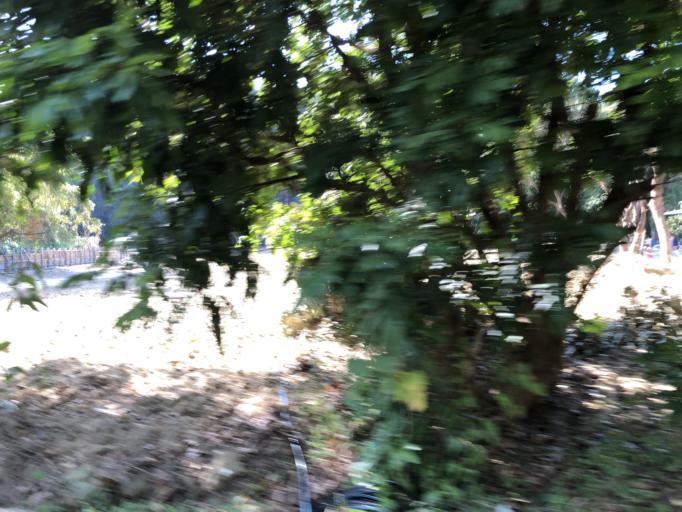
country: TW
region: Taiwan
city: Yujing
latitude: 23.0131
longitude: 120.3856
